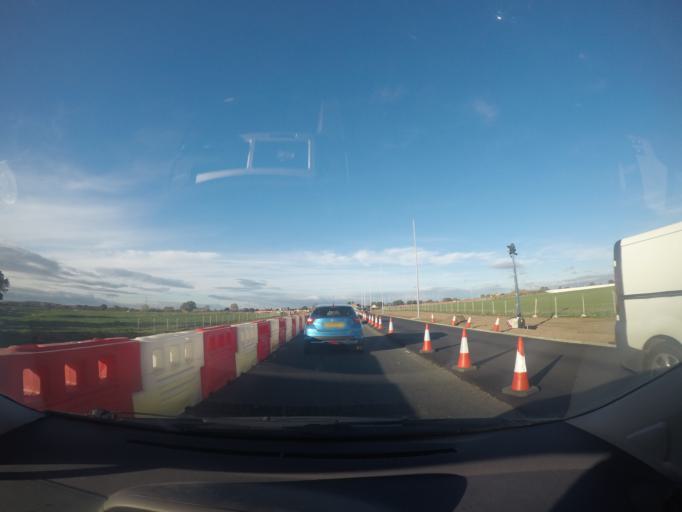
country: GB
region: England
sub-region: City of York
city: Nether Poppleton
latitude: 53.9540
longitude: -1.1492
